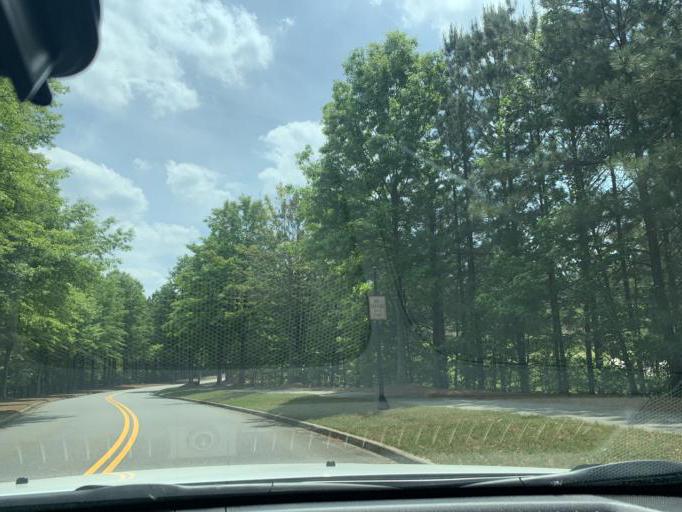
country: US
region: Georgia
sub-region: Forsyth County
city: Cumming
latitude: 34.1423
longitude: -84.1297
